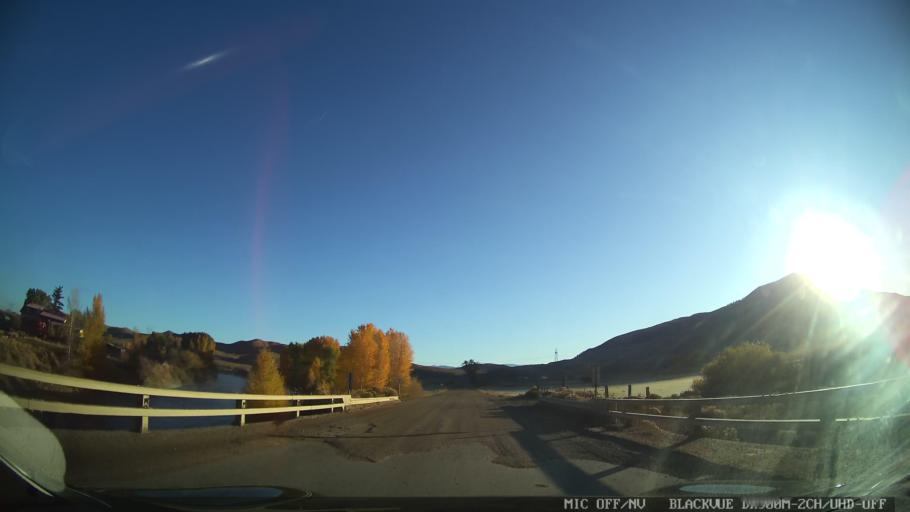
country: US
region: Colorado
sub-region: Grand County
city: Kremmling
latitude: 40.0287
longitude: -106.3872
